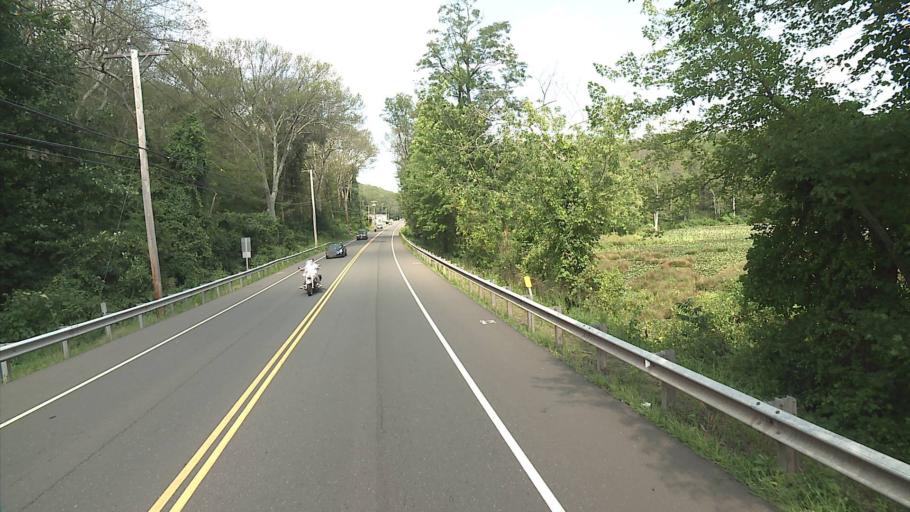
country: US
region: Connecticut
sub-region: Middlesex County
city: East Haddam
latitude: 41.4444
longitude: -72.4713
